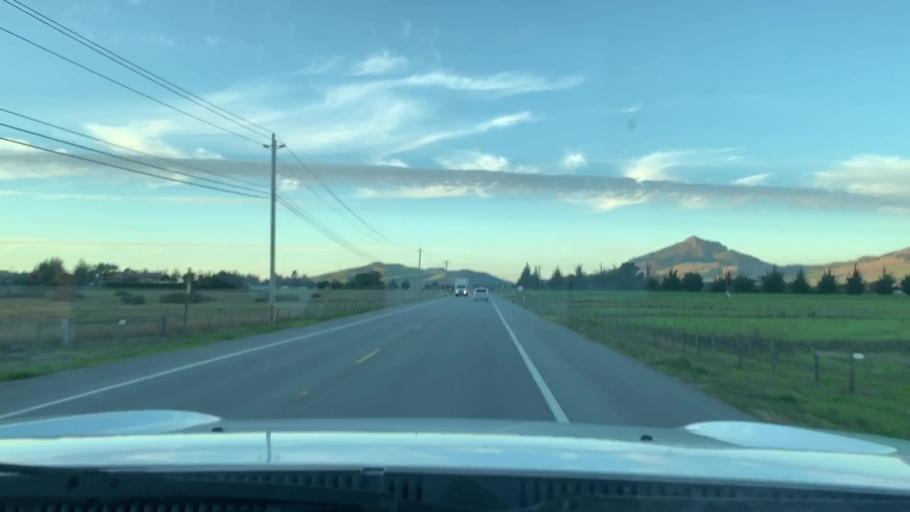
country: US
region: California
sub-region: San Luis Obispo County
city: San Luis Obispo
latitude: 35.2710
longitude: -120.7064
